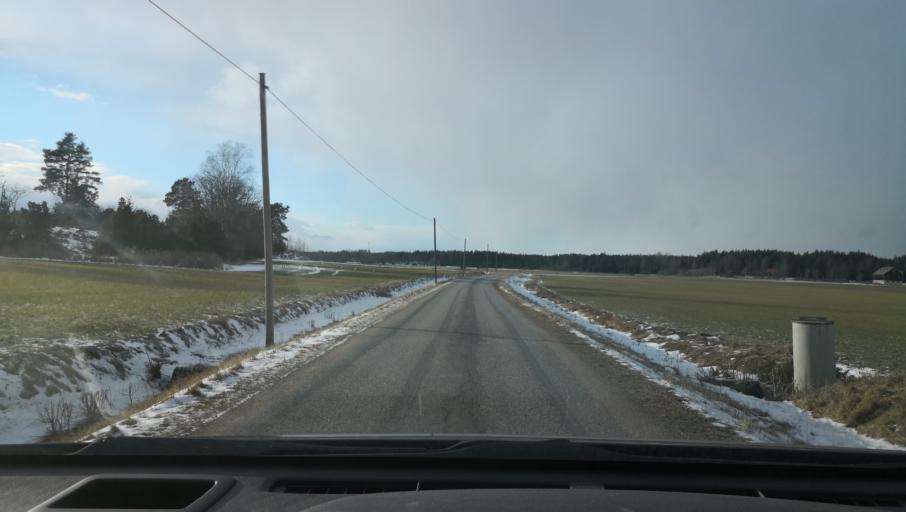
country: SE
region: Uppsala
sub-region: Enkopings Kommun
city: Irsta
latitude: 59.7050
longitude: 16.9203
